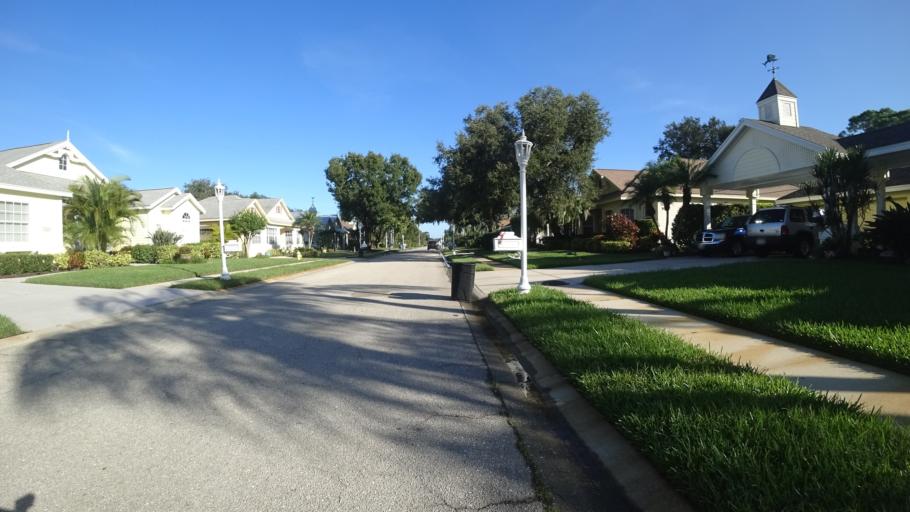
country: US
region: Florida
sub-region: Manatee County
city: Ellenton
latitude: 27.5006
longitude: -82.5025
